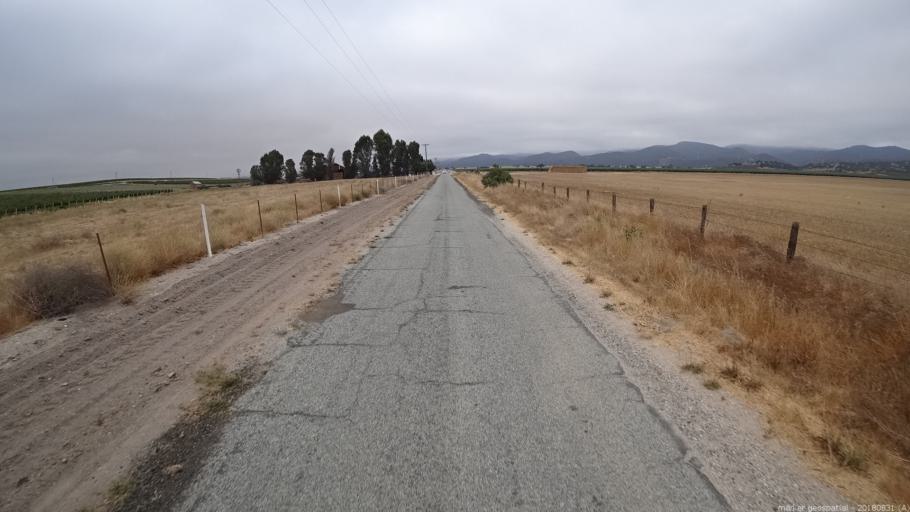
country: US
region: California
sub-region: Monterey County
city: King City
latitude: 36.1233
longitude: -121.0874
